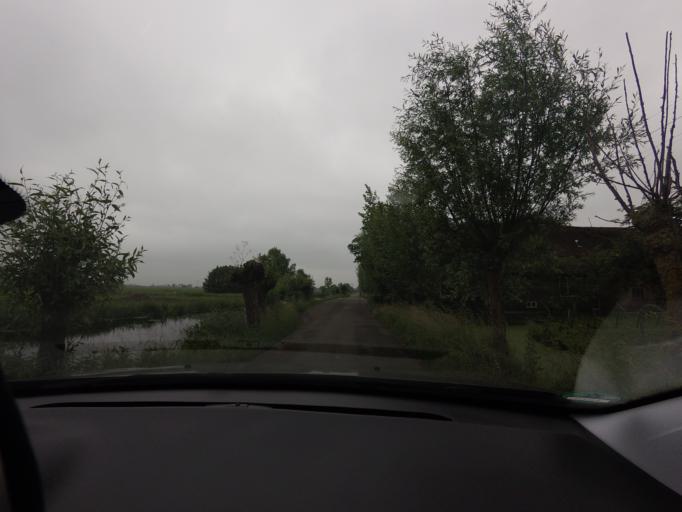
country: NL
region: South Holland
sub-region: Gemeente Vlist
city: Haastrecht
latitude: 52.0381
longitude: 4.7971
